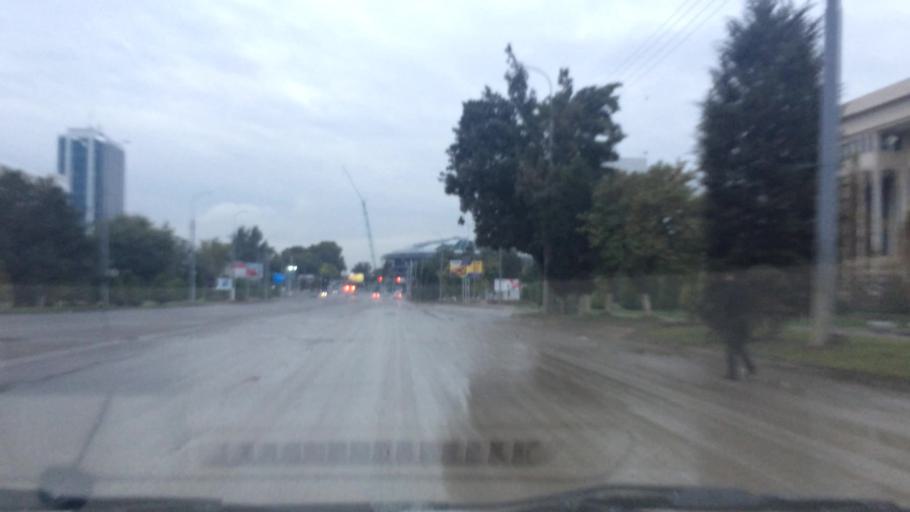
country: UZ
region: Toshkent Shahri
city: Tashkent
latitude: 41.3141
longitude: 69.2537
